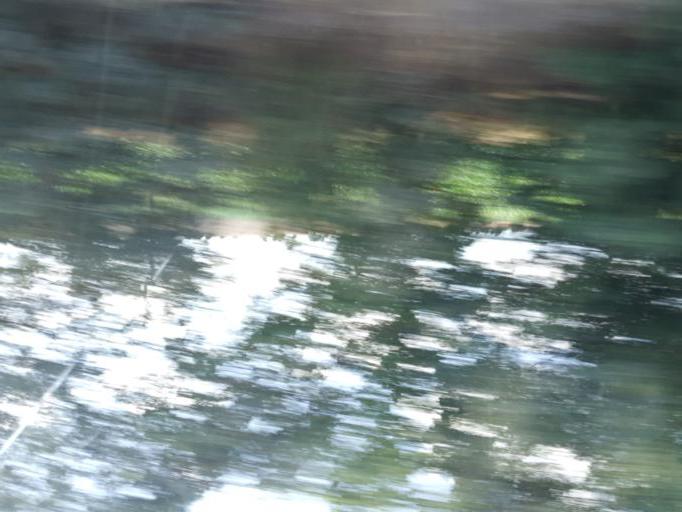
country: TR
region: Tokat
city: Sulusaray
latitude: 40.0014
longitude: 36.1289
